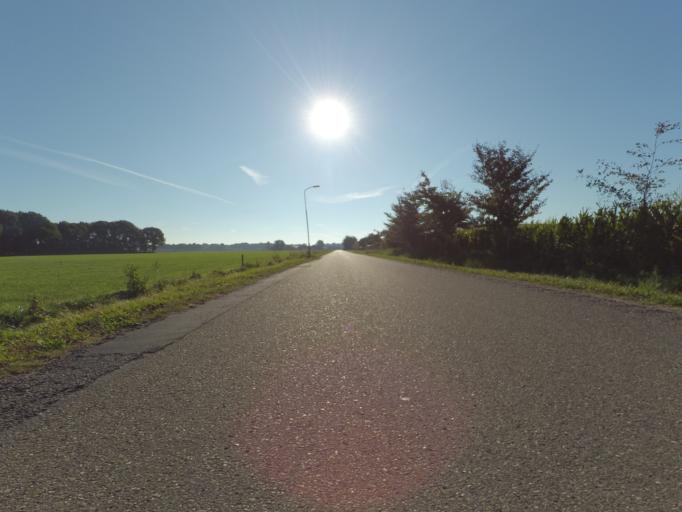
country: NL
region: Gelderland
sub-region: Gemeente Barneveld
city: Terschuur
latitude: 52.1999
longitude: 5.5536
